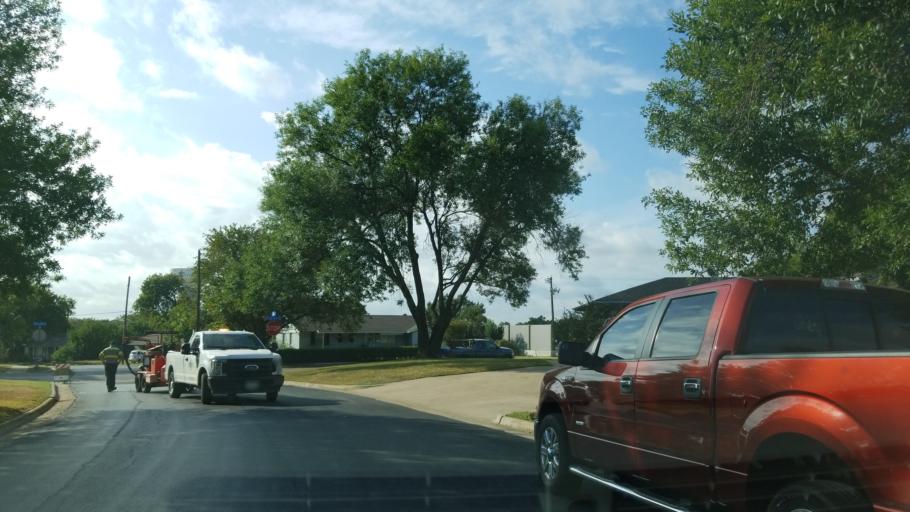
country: US
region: Texas
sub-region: Tarrant County
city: Euless
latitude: 32.8401
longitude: -97.0813
